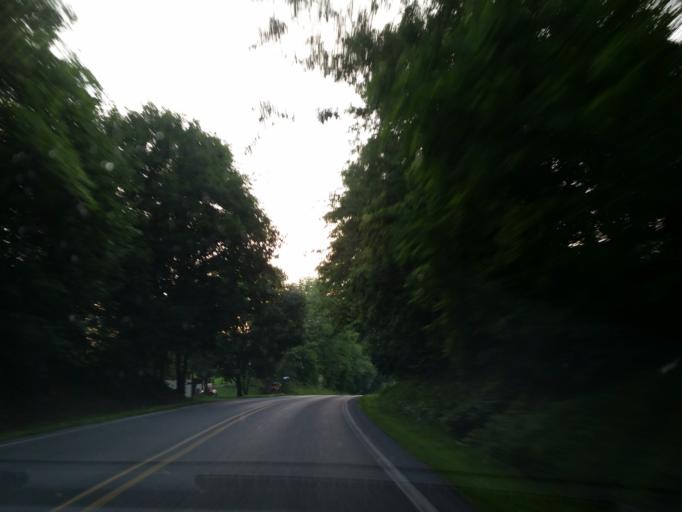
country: US
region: Pennsylvania
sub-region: Lebanon County
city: Jonestown
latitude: 40.4197
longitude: -76.5386
